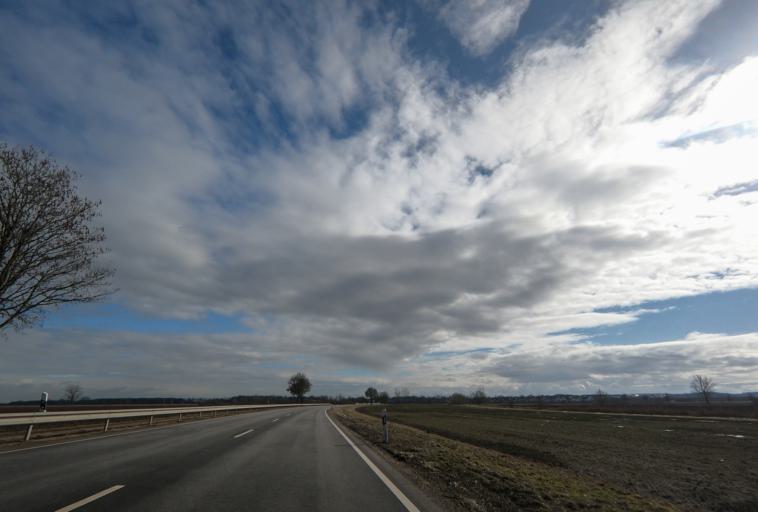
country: DE
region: Bavaria
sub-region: Upper Palatinate
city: Kofering
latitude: 48.9490
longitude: 12.1846
